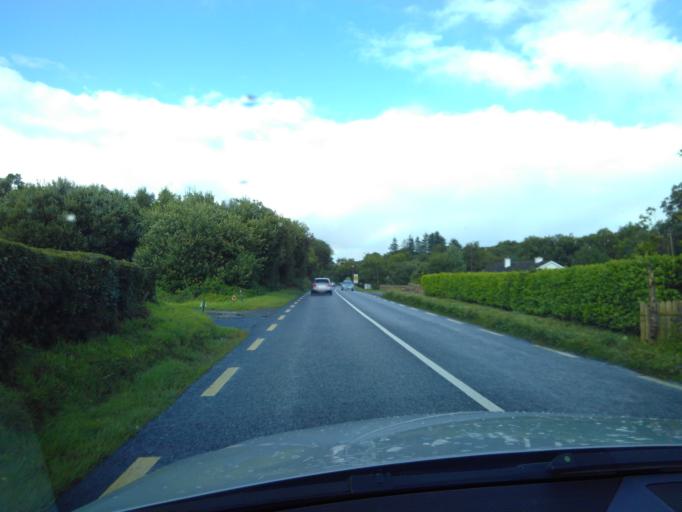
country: IE
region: Ulster
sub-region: County Donegal
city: Letterkenny
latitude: 54.9749
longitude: -7.6842
